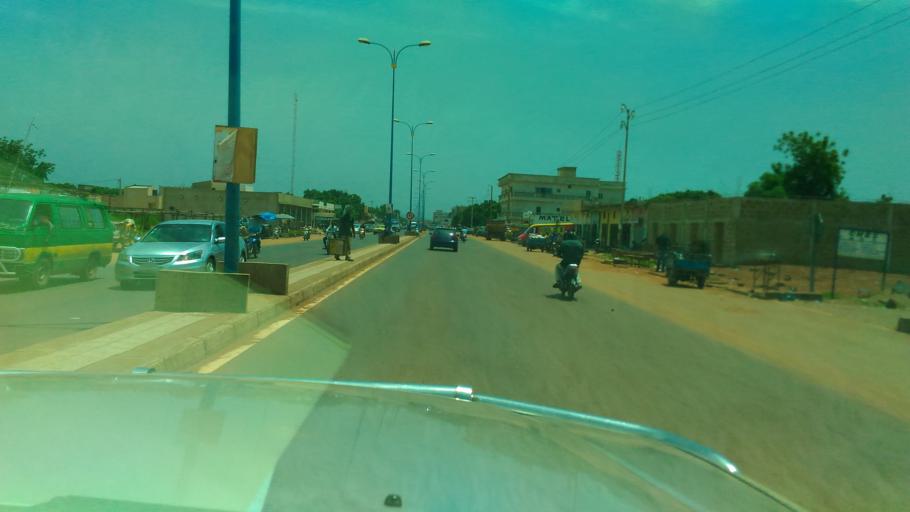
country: ML
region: Bamako
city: Bamako
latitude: 12.5980
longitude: -8.0557
